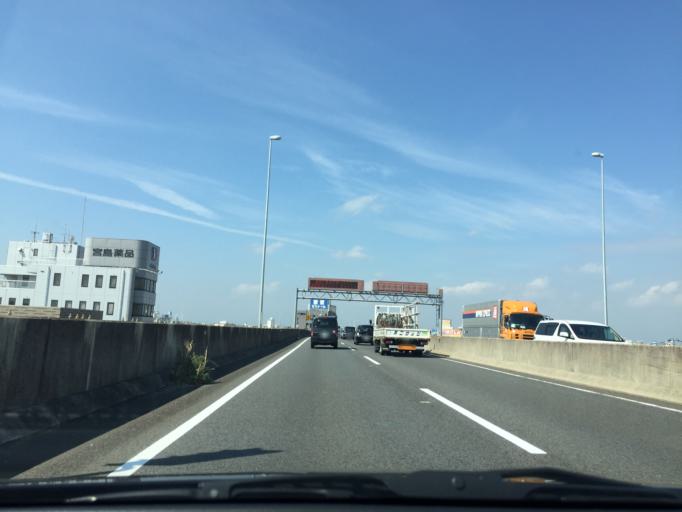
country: JP
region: Gifu
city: Kasamatsucho
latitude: 35.3892
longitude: 136.7982
